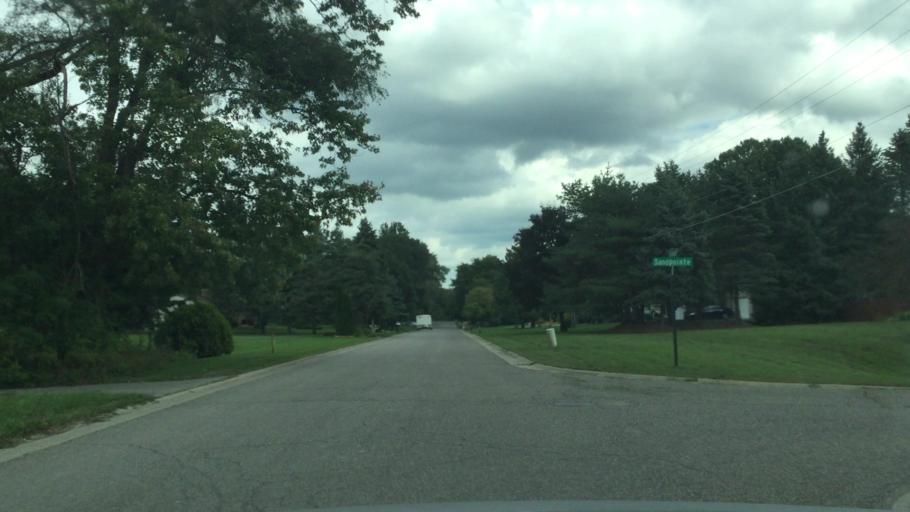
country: US
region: Michigan
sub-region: Livingston County
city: Brighton
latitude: 42.5581
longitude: -83.7456
